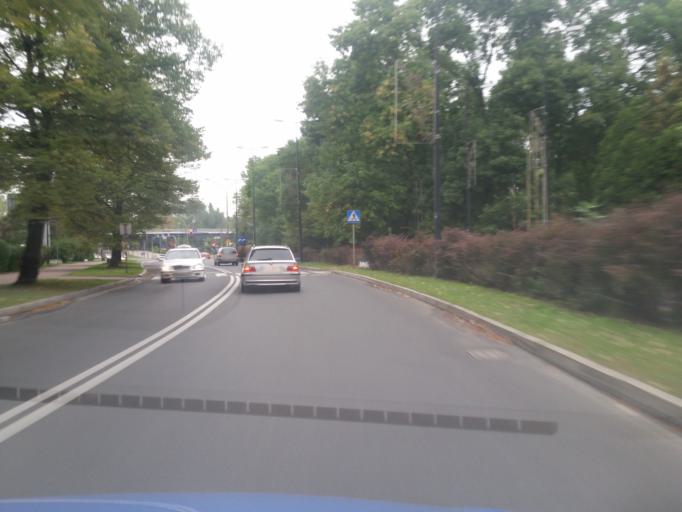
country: PL
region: Silesian Voivodeship
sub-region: Sosnowiec
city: Sosnowiec
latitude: 50.2794
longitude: 19.1352
